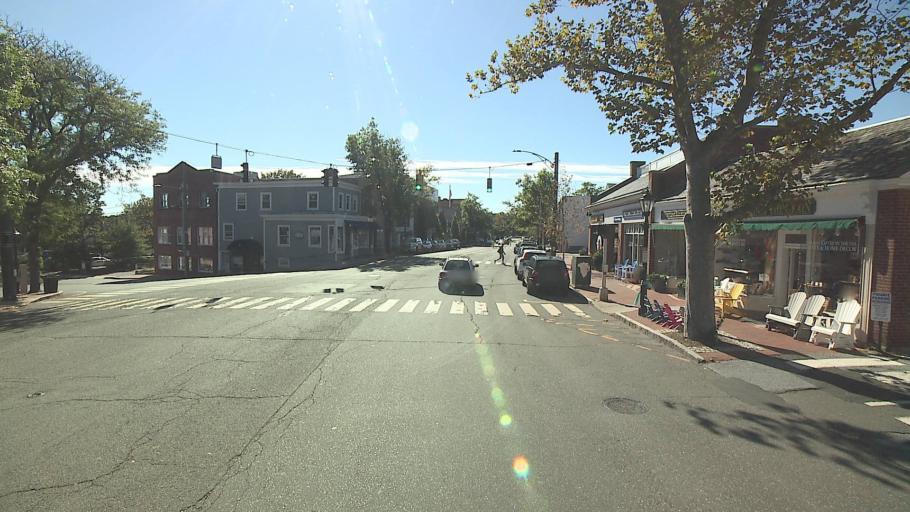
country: US
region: Connecticut
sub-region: Fairfield County
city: New Canaan
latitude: 41.1478
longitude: -73.4926
